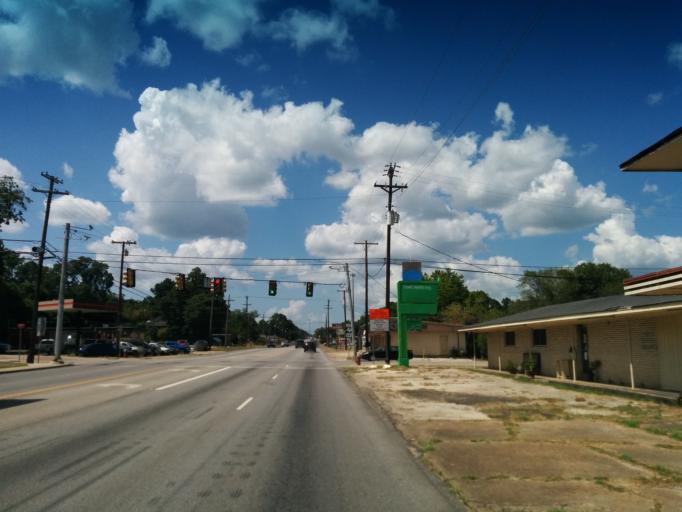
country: US
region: Texas
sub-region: Jasper County
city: Jasper
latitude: 30.9225
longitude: -93.9968
